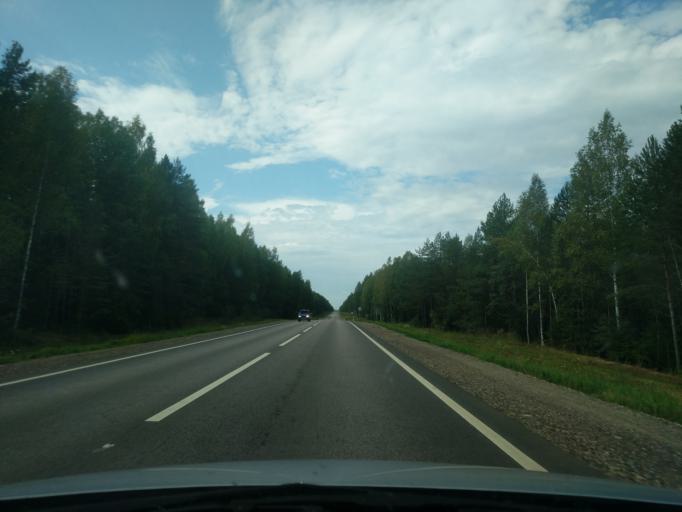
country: RU
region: Kostroma
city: Kadyy
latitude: 57.7947
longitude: 42.9553
